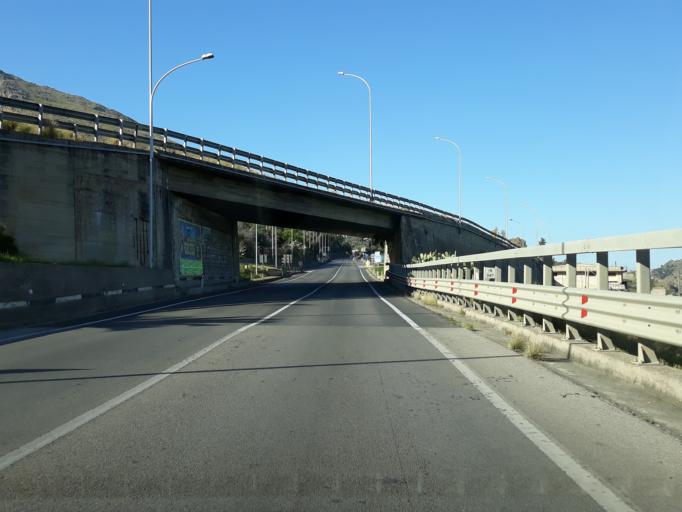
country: IT
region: Sicily
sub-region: Palermo
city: Misilmeri
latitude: 38.0429
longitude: 13.4607
